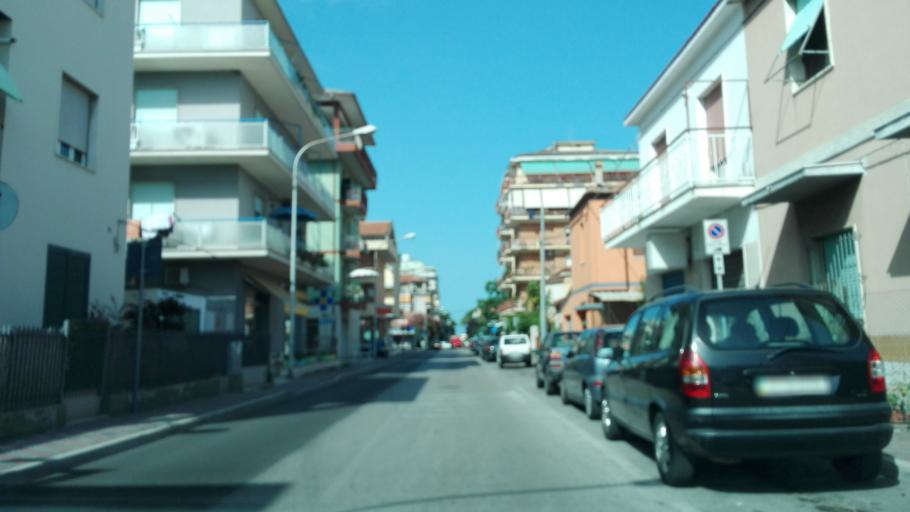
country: IT
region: Abruzzo
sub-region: Provincia di Pescara
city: Montesilvano Marina
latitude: 42.4974
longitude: 14.1750
